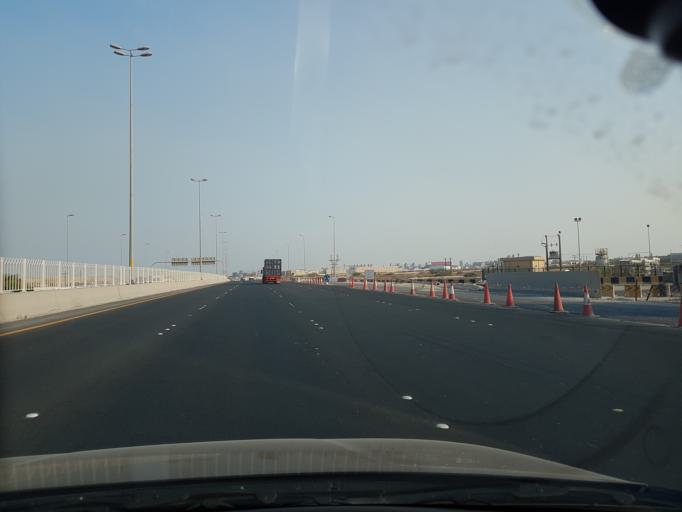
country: BH
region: Northern
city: Ar Rifa'
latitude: 26.1151
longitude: 50.5951
